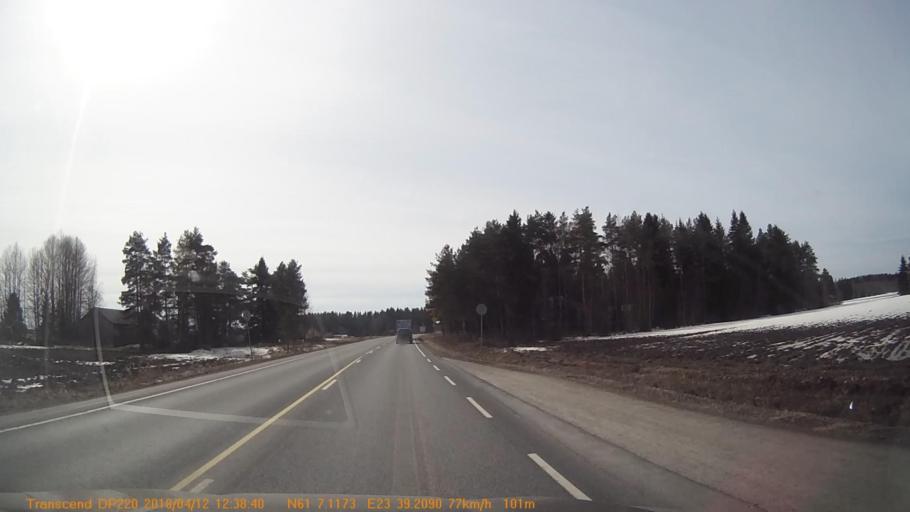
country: FI
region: Pirkanmaa
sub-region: Etelae-Pirkanmaa
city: Kylmaekoski
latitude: 61.1188
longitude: 23.6537
